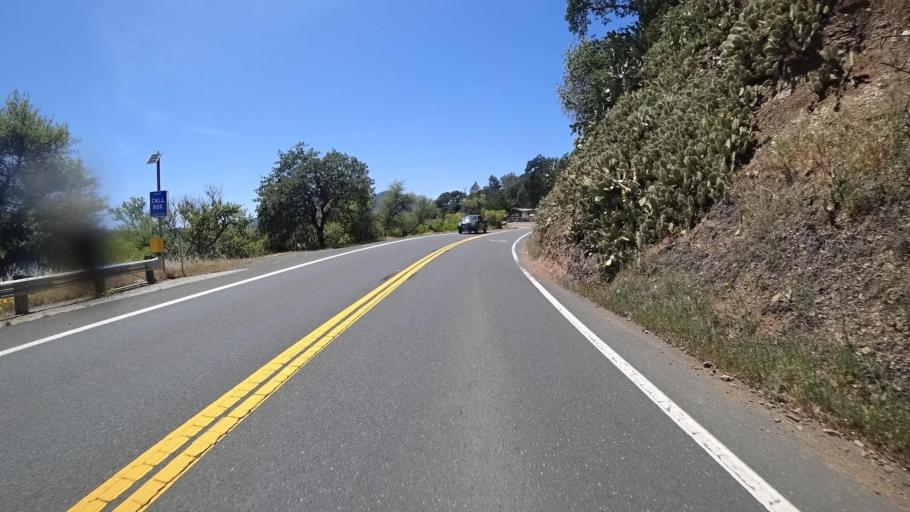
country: US
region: California
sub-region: Lake County
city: Clearlake Oaks
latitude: 39.0206
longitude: -122.6834
